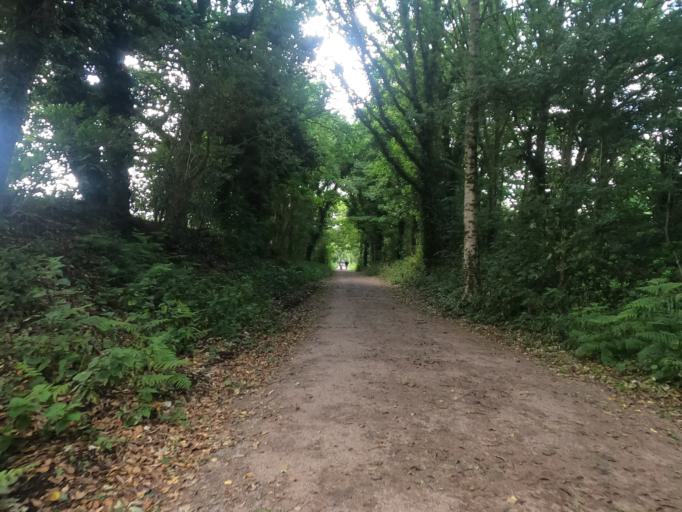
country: GB
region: England
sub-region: Cheshire West and Chester
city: Over
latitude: 53.2059
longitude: -2.5725
